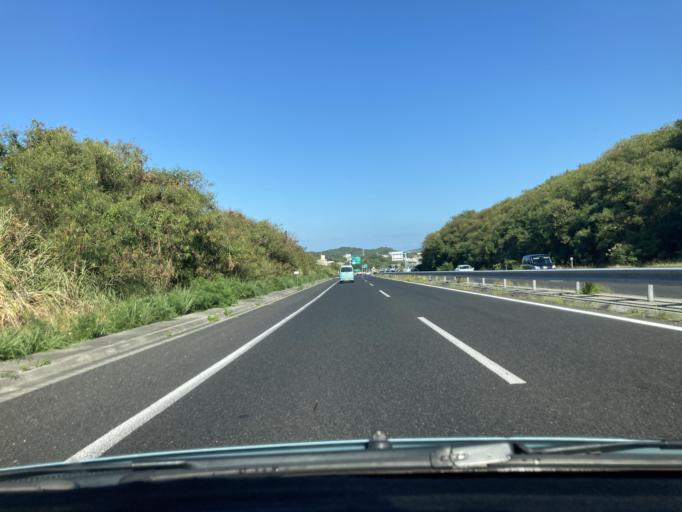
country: JP
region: Okinawa
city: Tomigusuku
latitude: 26.1763
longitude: 127.7078
